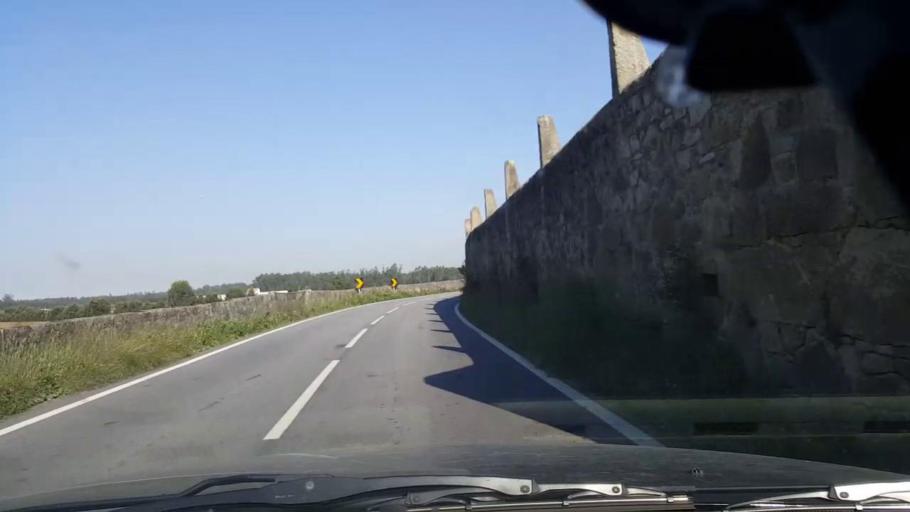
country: PT
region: Porto
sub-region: Vila do Conde
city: Arvore
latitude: 41.3208
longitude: -8.6799
